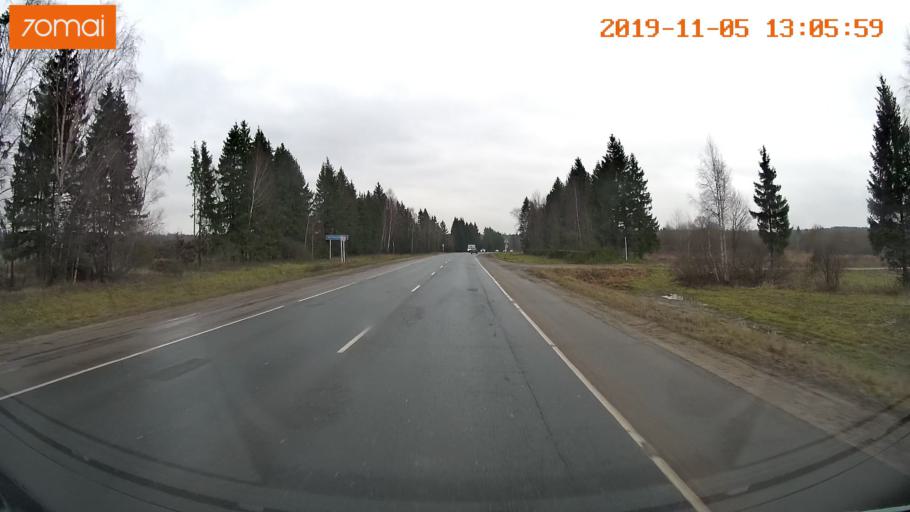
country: RU
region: Ivanovo
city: Kitovo
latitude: 56.8790
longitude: 41.2547
